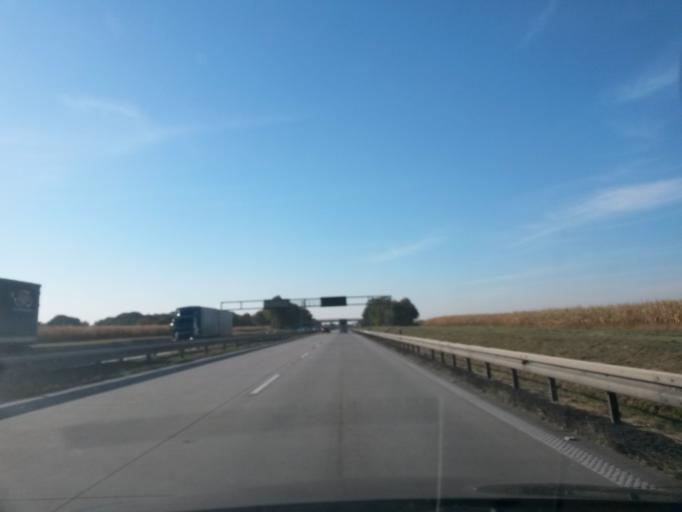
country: PL
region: Lower Silesian Voivodeship
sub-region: Powiat sredzki
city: Udanin
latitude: 51.0787
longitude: 16.4412
